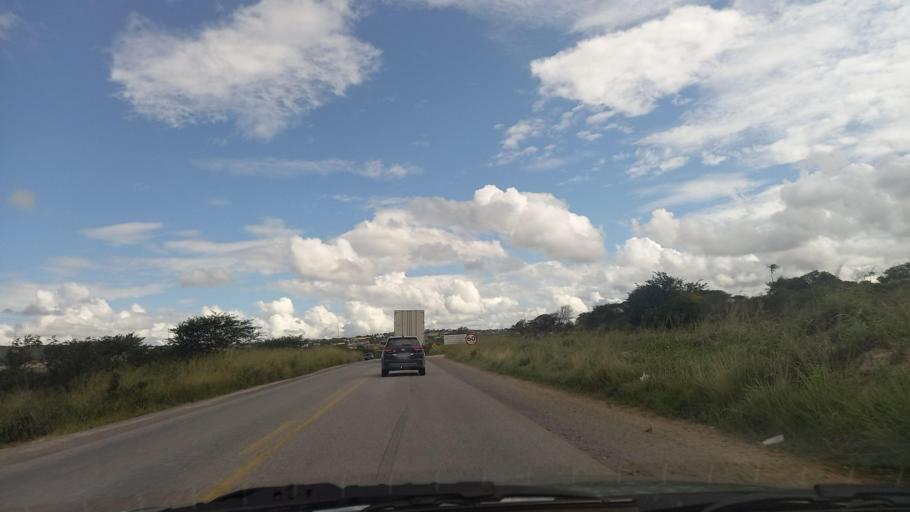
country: BR
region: Pernambuco
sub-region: Lajedo
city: Lajedo
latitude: -8.6937
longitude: -36.4124
